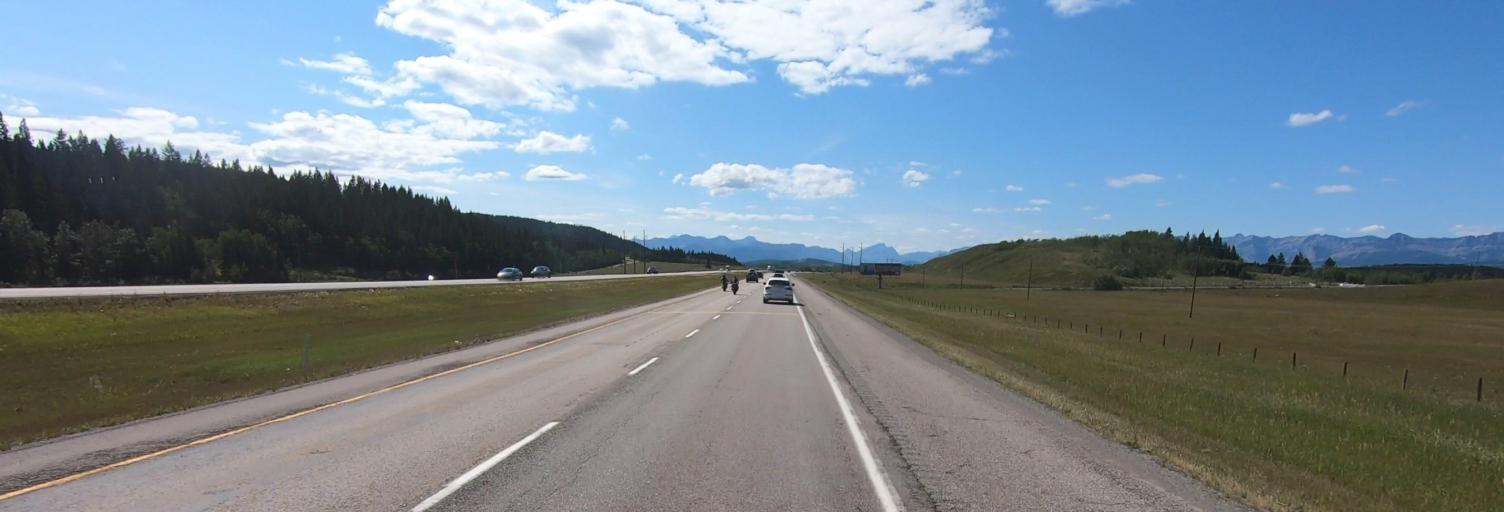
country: CA
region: Alberta
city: Cochrane
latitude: 51.1538
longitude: -114.8068
